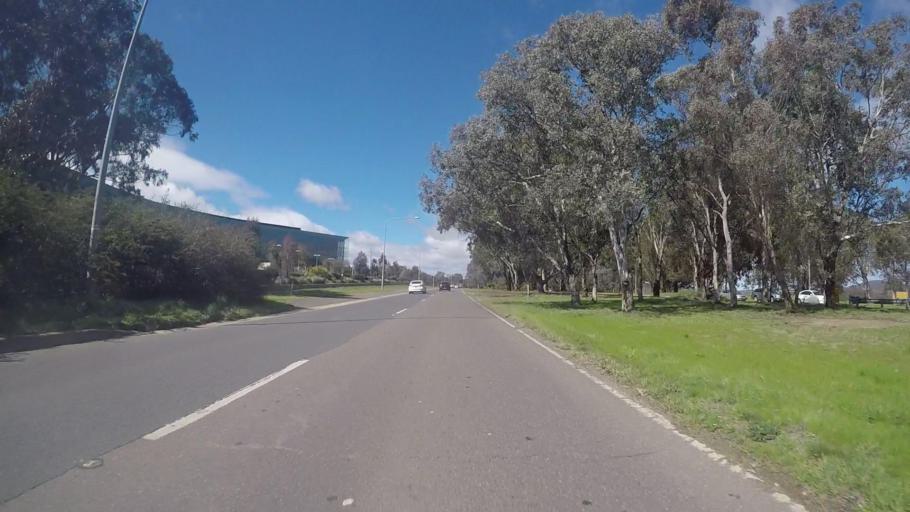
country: AU
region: Australian Capital Territory
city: Canberra
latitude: -35.2925
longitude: 149.1427
